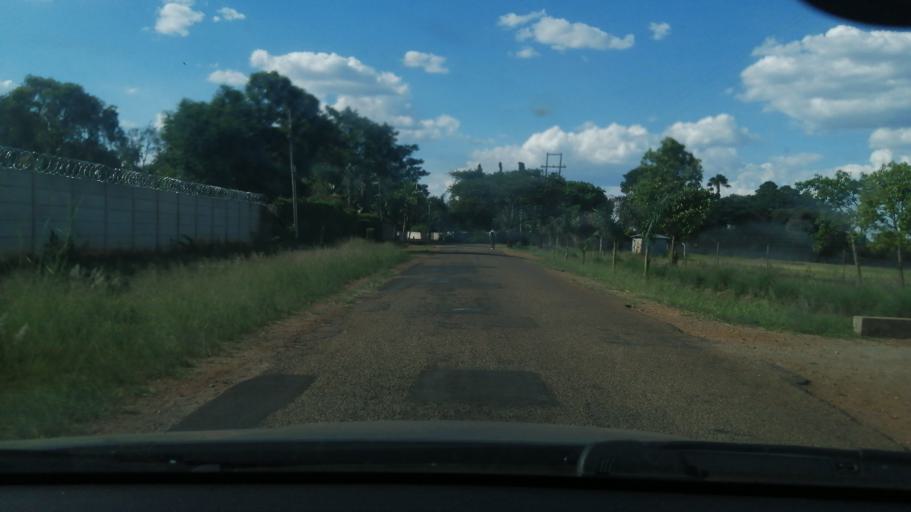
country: ZW
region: Harare
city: Harare
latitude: -17.7692
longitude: 31.0625
